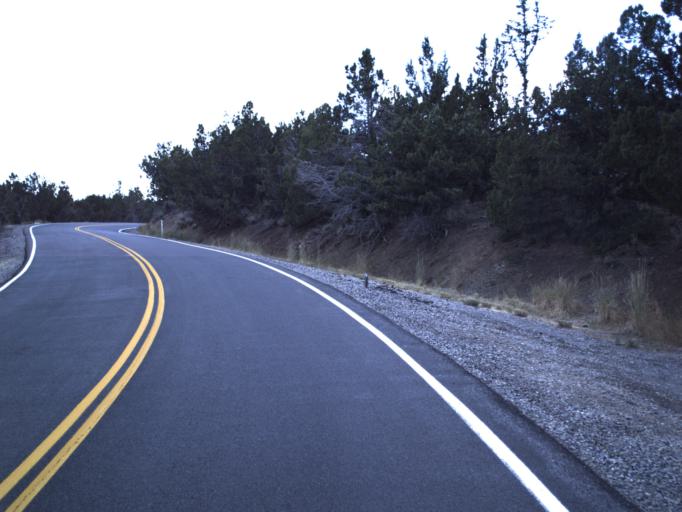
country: US
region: Utah
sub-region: Tooele County
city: Grantsville
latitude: 40.3415
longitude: -112.5673
